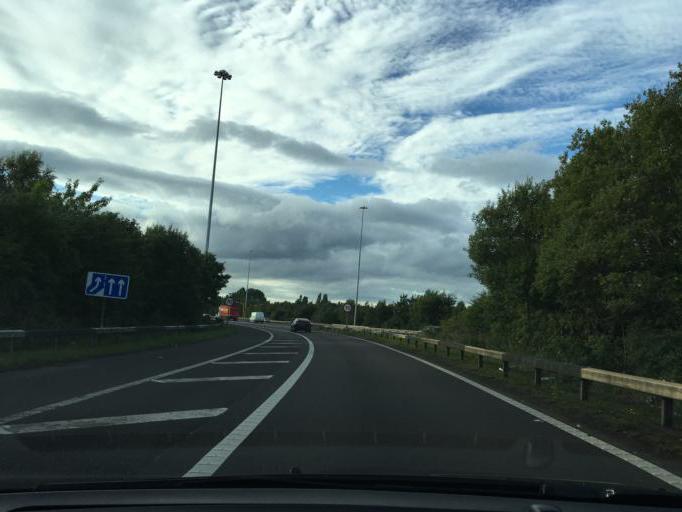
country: GB
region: Scotland
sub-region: South Lanarkshire
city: Hamilton
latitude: 55.7807
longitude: -4.0225
